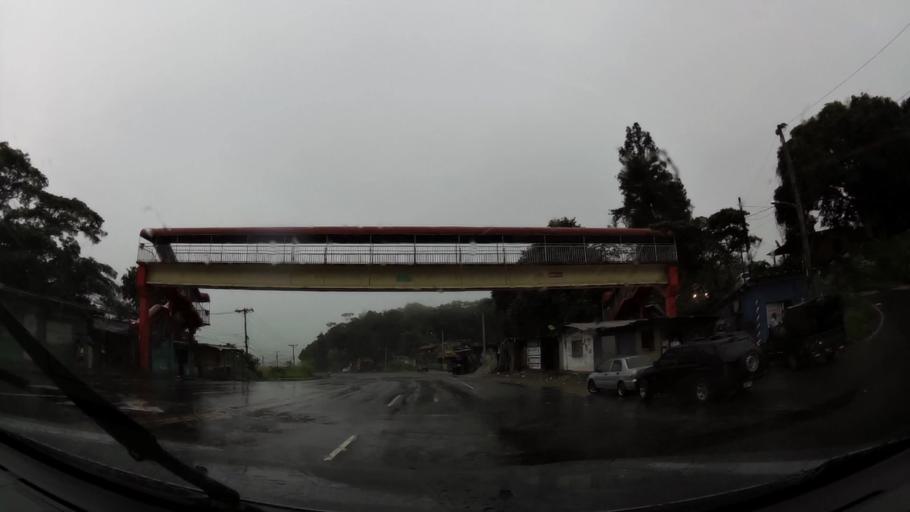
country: PA
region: Colon
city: Rio Rita
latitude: 9.3094
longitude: -79.7912
